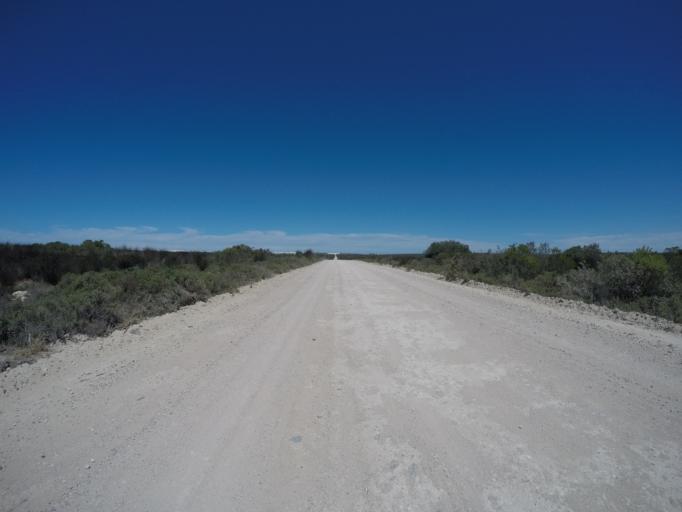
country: ZA
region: Western Cape
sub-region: Overberg District Municipality
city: Bredasdorp
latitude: -34.4500
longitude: 20.4232
